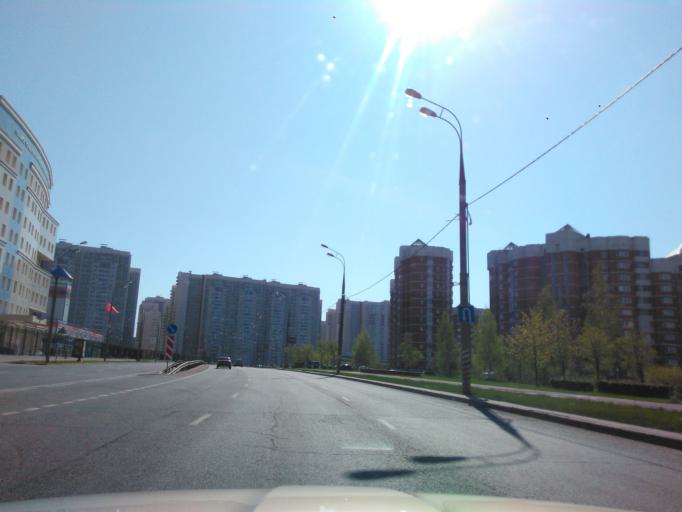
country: RU
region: Moscow
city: Khimki
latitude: 55.9018
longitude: 37.3926
